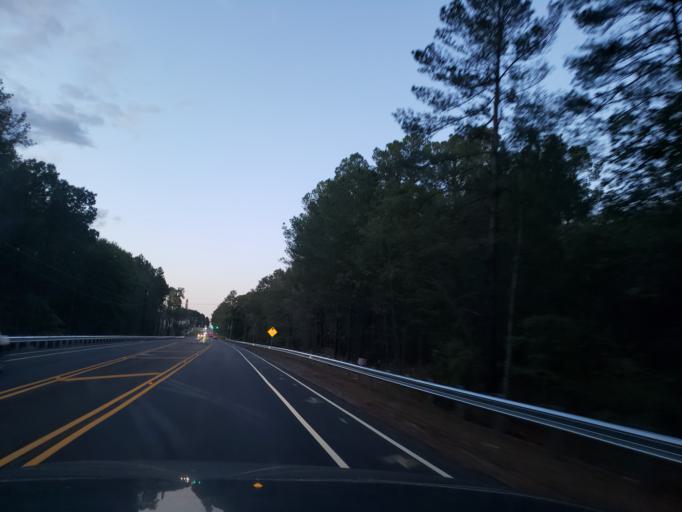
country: US
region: North Carolina
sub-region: Orange County
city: Chapel Hill
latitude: 35.8854
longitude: -78.9567
